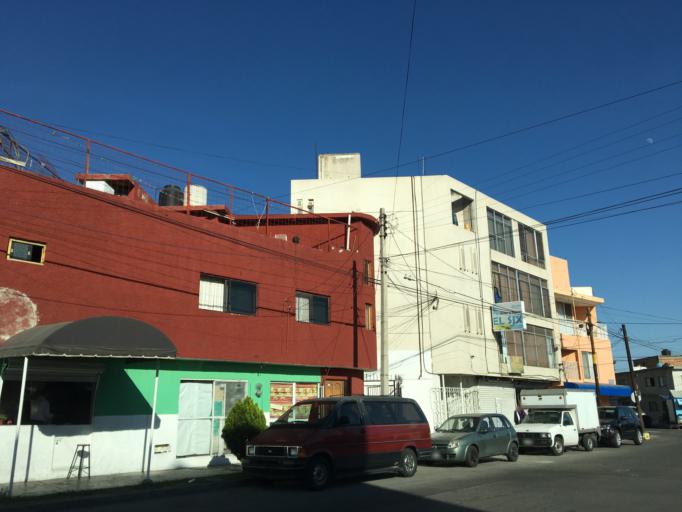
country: MX
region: San Luis Potosi
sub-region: San Luis Potosi
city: San Luis Potosi
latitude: 22.1445
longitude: -100.9897
